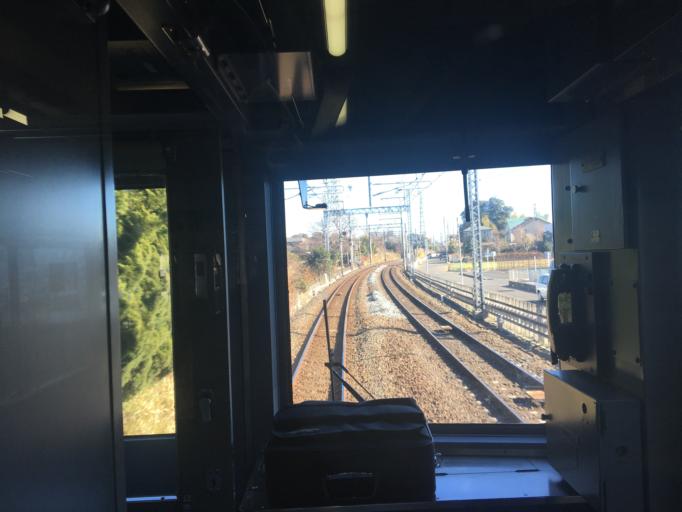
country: JP
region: Saitama
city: Iwatsuki
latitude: 35.9379
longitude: 139.6679
